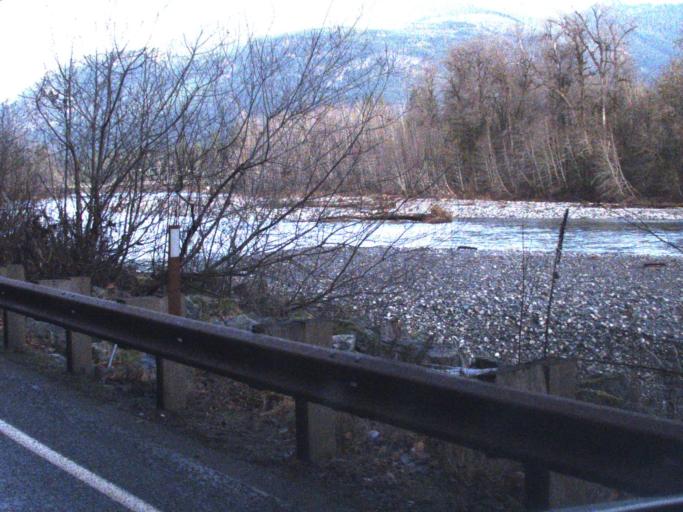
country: US
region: Washington
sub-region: Snohomish County
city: Darrington
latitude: 48.3389
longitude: -121.5511
